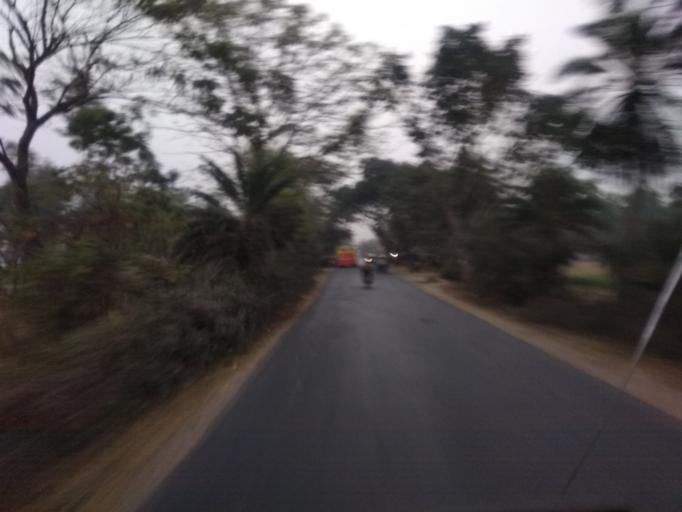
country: BD
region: Rajshahi
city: Bogra
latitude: 24.7361
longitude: 89.3288
